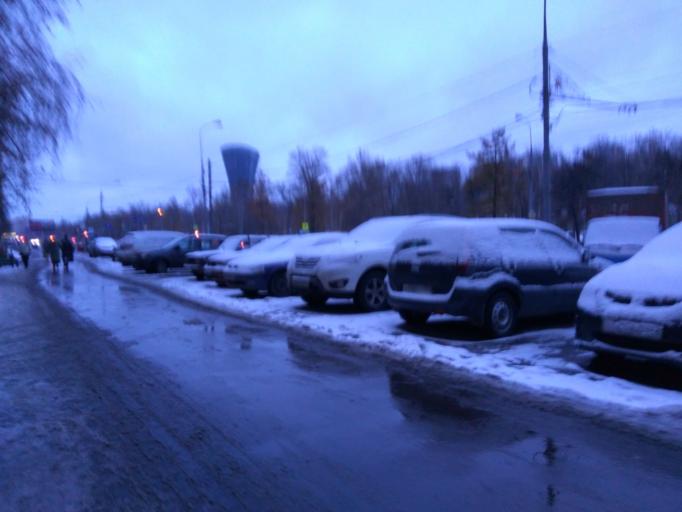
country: RU
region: Moscow
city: Sokol
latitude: 55.7829
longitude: 37.5142
